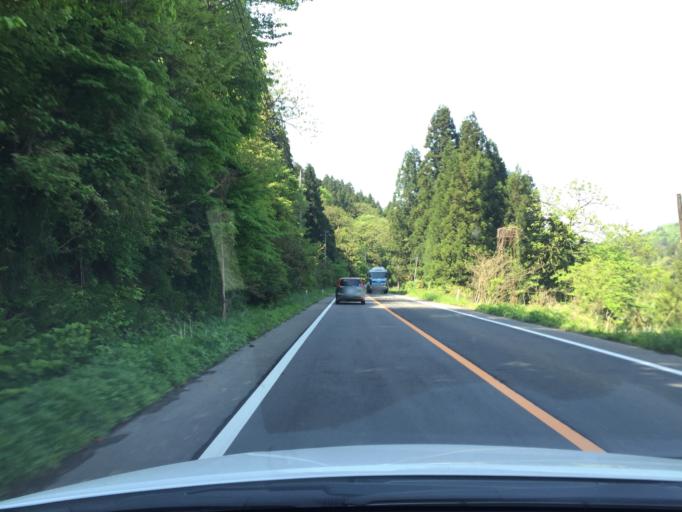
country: JP
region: Niigata
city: Muramatsu
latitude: 37.6526
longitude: 139.1361
